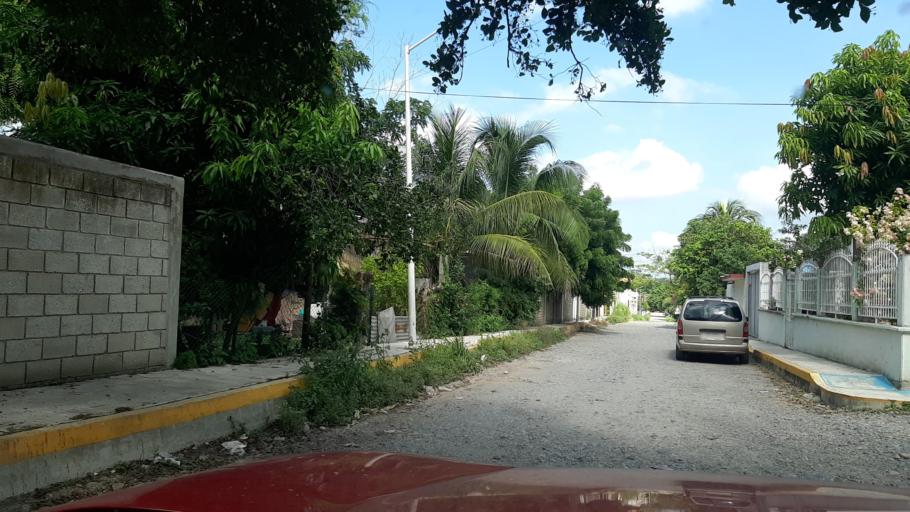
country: MX
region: Veracruz
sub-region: Poza Rica de Hidalgo
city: Villa de las Flores
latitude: 20.5744
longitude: -97.4328
